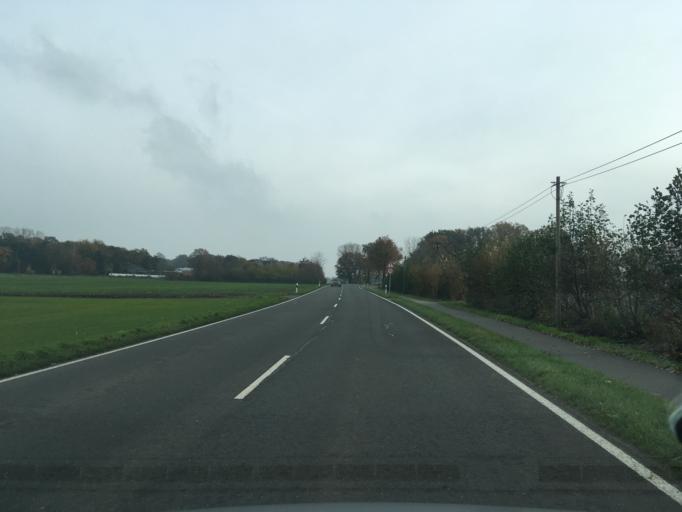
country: DE
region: North Rhine-Westphalia
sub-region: Regierungsbezirk Munster
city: Sudlohn
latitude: 51.9549
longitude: 6.8505
